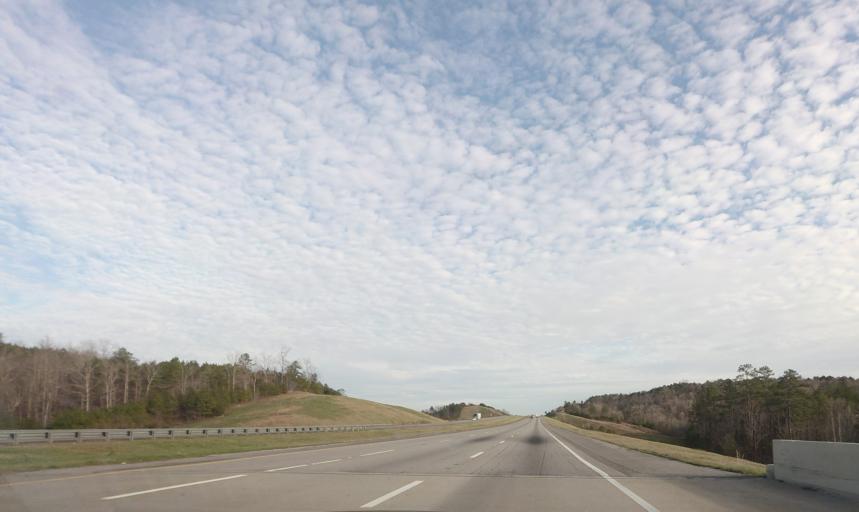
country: US
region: Alabama
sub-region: Walker County
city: Dora
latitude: 33.6852
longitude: -87.1028
